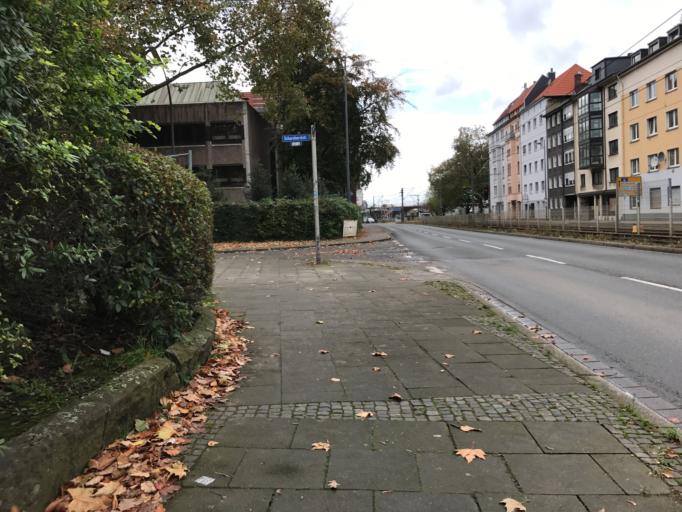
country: DE
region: North Rhine-Westphalia
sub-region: Regierungsbezirk Arnsberg
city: Dortmund
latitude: 51.5240
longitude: 7.4464
